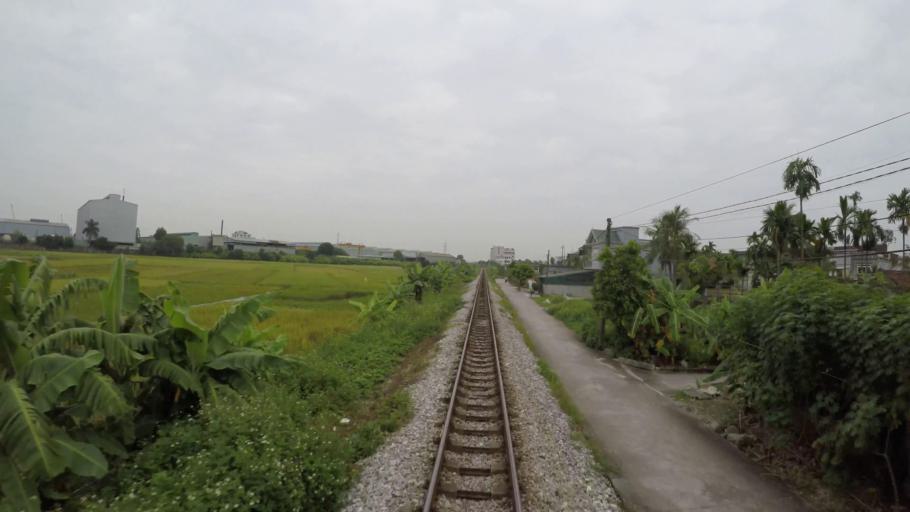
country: VN
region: Hai Phong
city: An Duong
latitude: 20.9003
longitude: 106.5788
